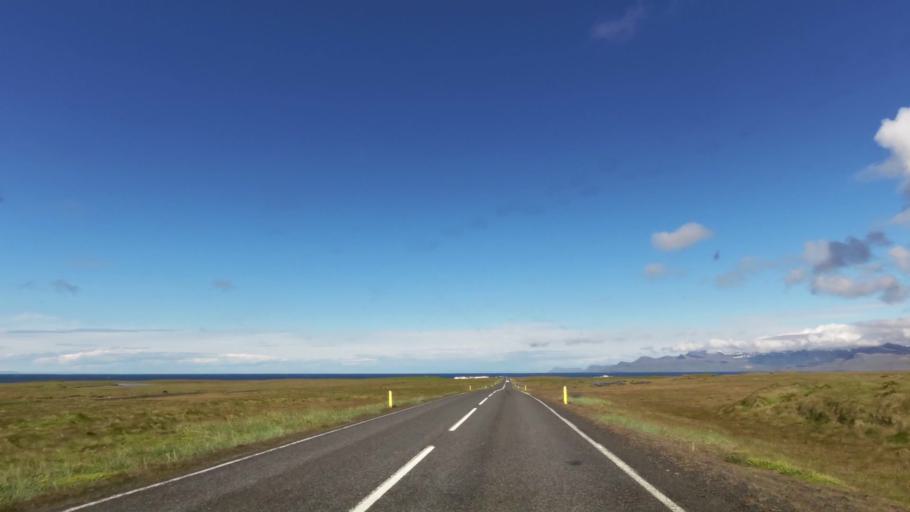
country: IS
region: West
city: Olafsvik
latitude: 64.9171
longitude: -23.8531
